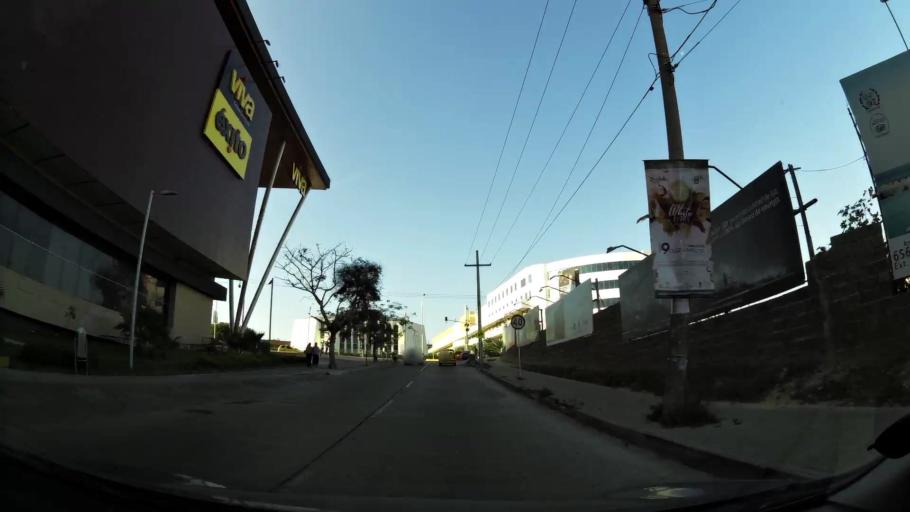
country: CO
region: Atlantico
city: Barranquilla
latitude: 11.0086
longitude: -74.8218
